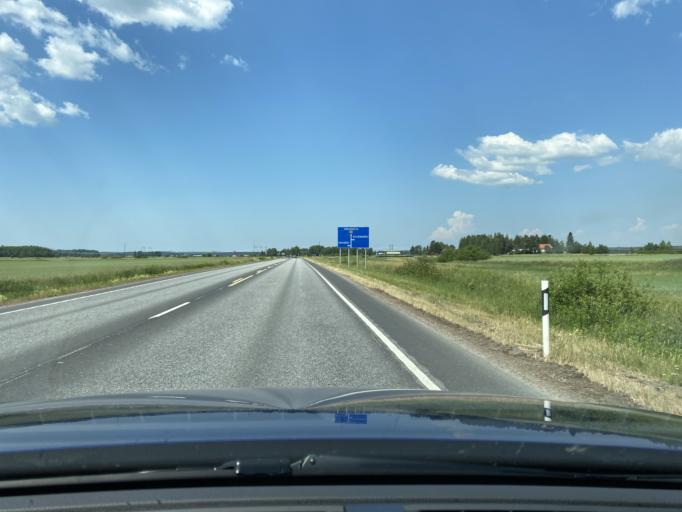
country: FI
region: Satakunta
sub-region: Rauma
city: Eura
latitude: 61.1536
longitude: 22.0958
